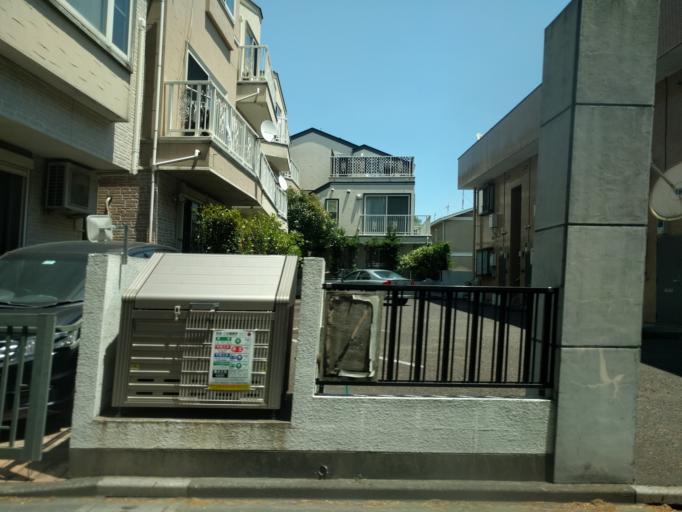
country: JP
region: Tokyo
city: Chofugaoka
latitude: 35.6510
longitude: 139.5966
